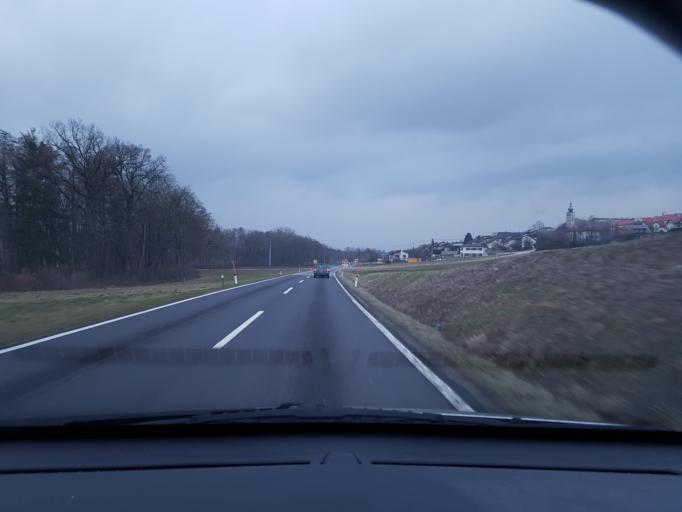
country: AT
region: Upper Austria
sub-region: Politischer Bezirk Linz-Land
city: Sankt Florian
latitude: 48.1559
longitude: 14.3328
